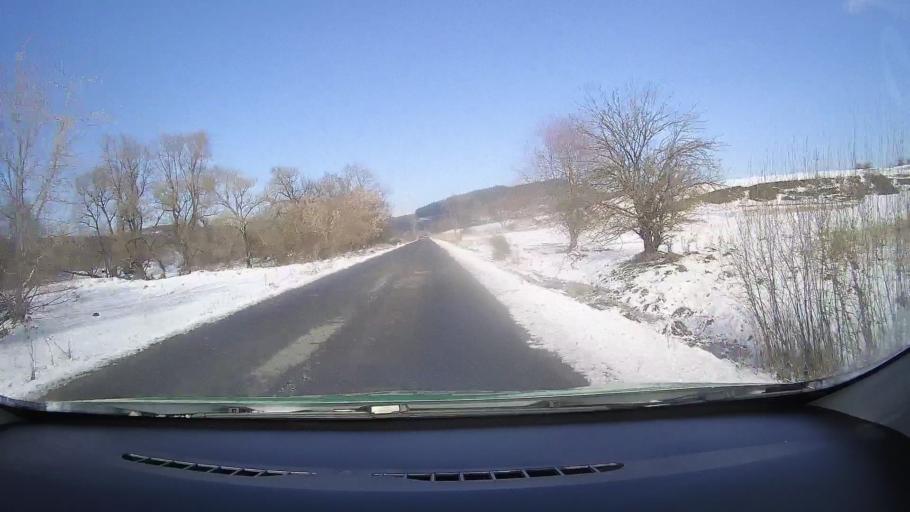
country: RO
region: Sibiu
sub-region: Comuna Mihaileni
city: Mihaileni
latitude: 46.0006
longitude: 24.3615
